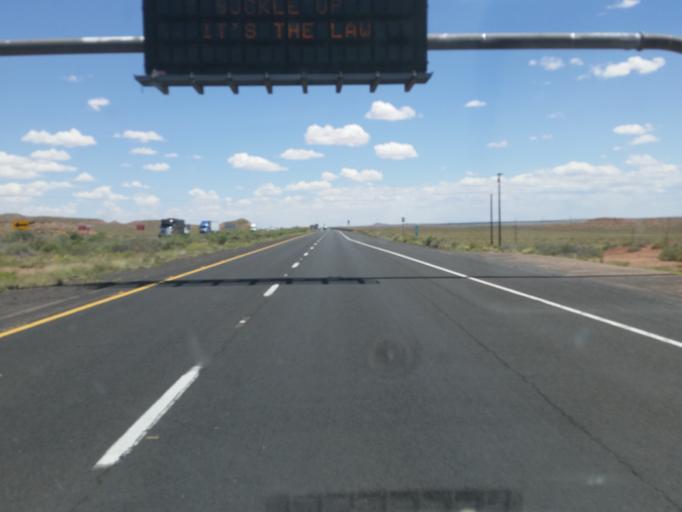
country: US
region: Arizona
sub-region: Navajo County
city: Joseph City
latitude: 34.9200
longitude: -110.2567
